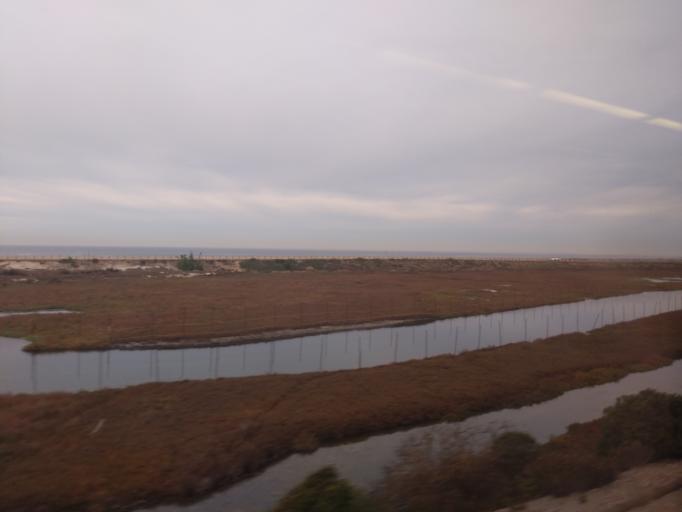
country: US
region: California
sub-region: San Diego County
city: Solana Beach
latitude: 33.0070
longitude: -117.2766
